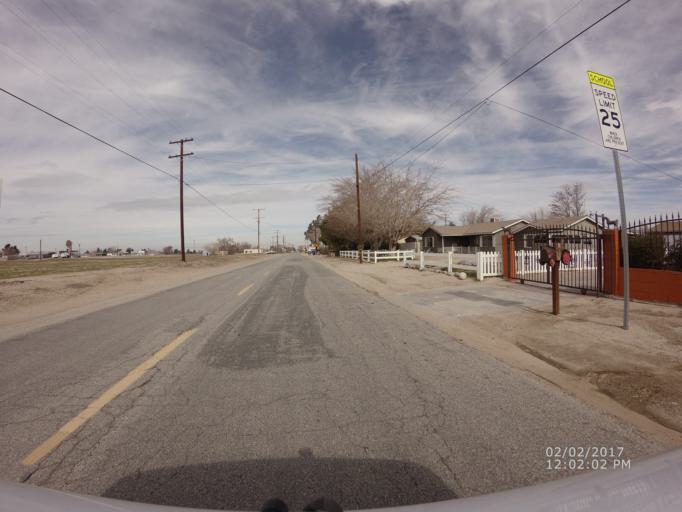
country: US
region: California
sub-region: Los Angeles County
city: Littlerock
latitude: 34.5189
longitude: -117.9837
